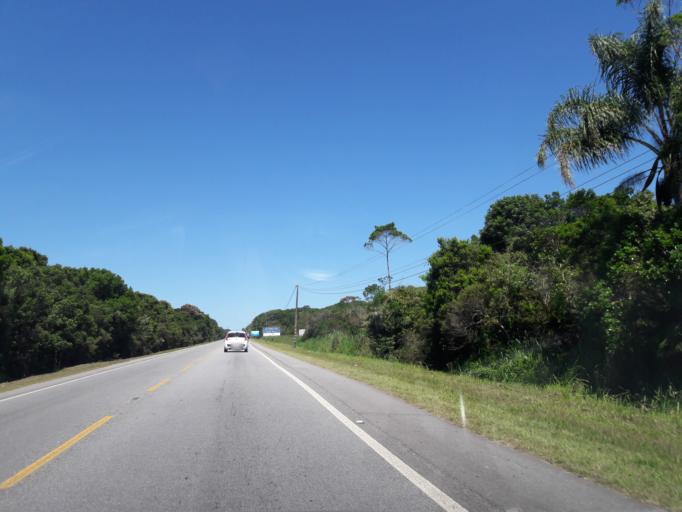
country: BR
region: Parana
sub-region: Pontal Do Parana
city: Pontal do Parana
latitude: -25.6801
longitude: -48.5010
